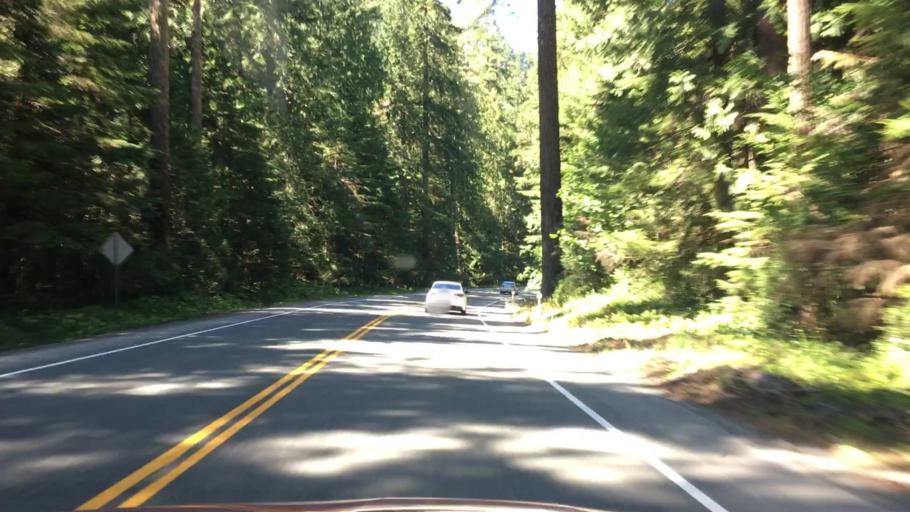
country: CA
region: British Columbia
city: Port Alberni
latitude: 49.2693
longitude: -124.6746
